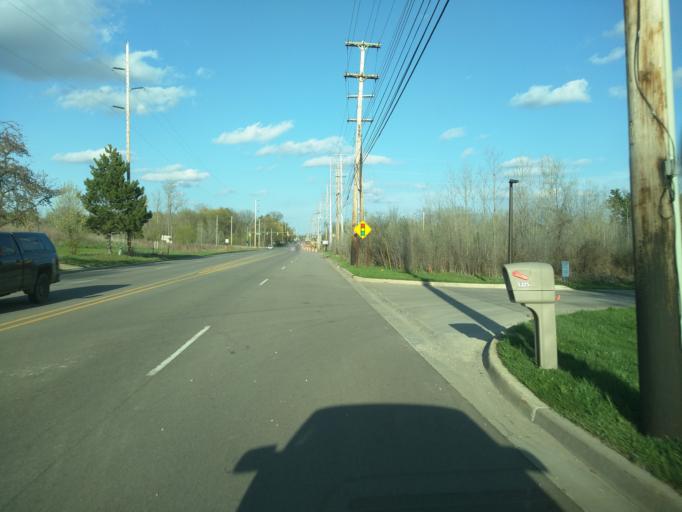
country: US
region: Michigan
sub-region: Eaton County
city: Waverly
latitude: 42.7120
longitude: -84.6256
